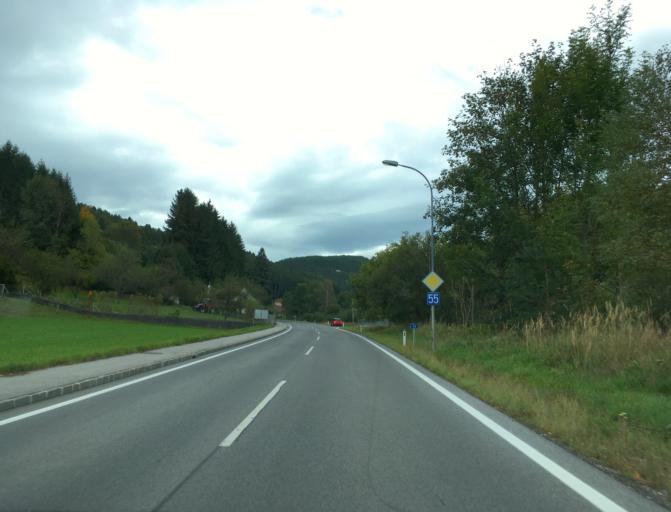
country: AT
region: Lower Austria
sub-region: Politischer Bezirk Neunkirchen
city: Edlitz
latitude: 47.5916
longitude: 16.1456
